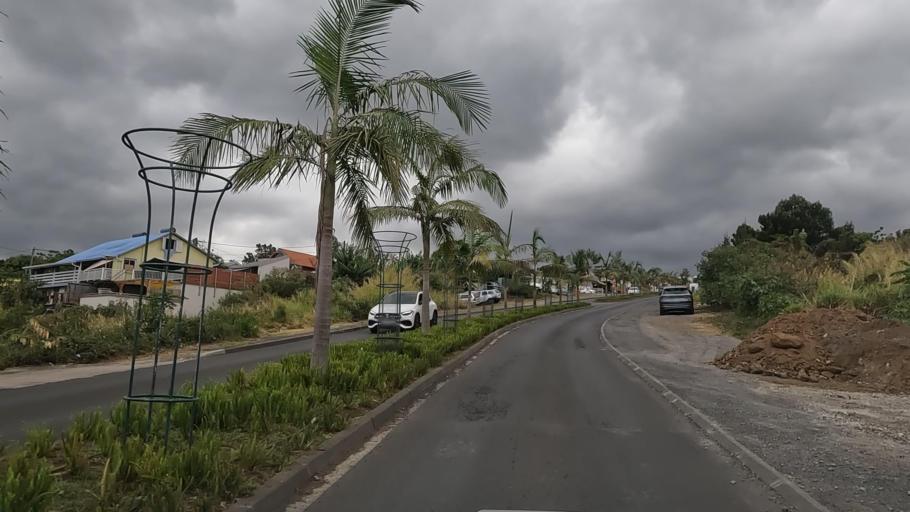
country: RE
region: Reunion
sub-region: Reunion
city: Le Tampon
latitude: -21.2653
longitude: 55.5125
